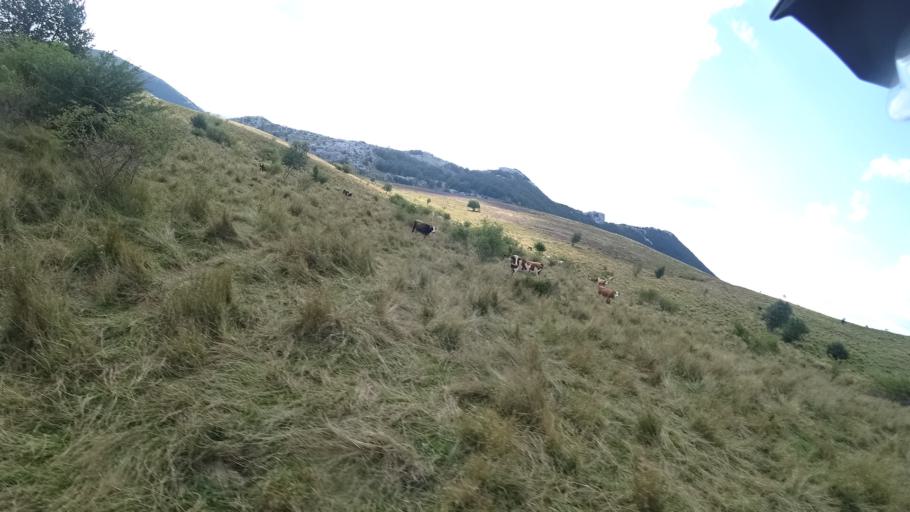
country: HR
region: Zadarska
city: Gracac
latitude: 44.4163
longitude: 16.0017
